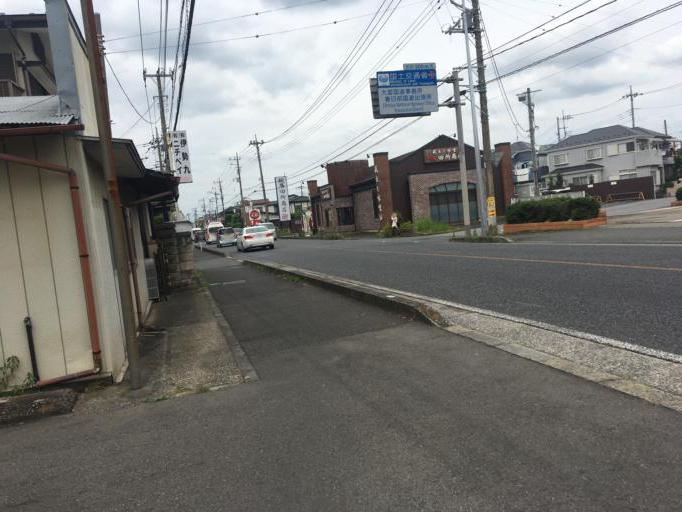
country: JP
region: Saitama
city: Kasukabe
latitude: 35.9764
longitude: 139.7645
